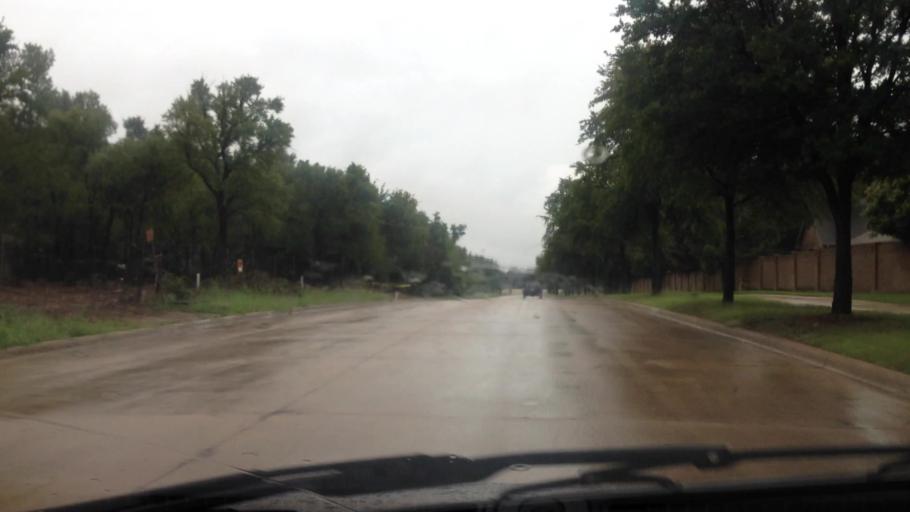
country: US
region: Texas
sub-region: Tarrant County
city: Keller
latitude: 32.9112
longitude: -97.2107
